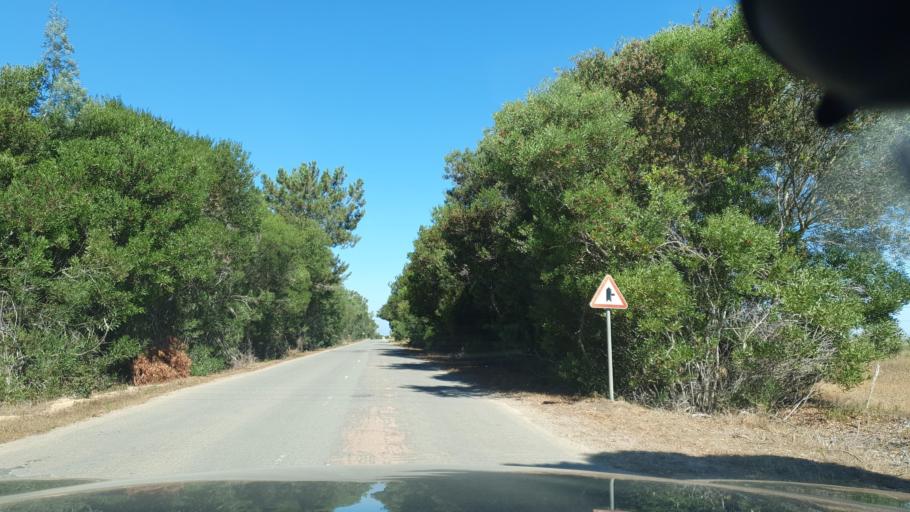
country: PT
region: Beja
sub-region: Odemira
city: Sao Teotonio
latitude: 37.4997
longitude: -8.6849
